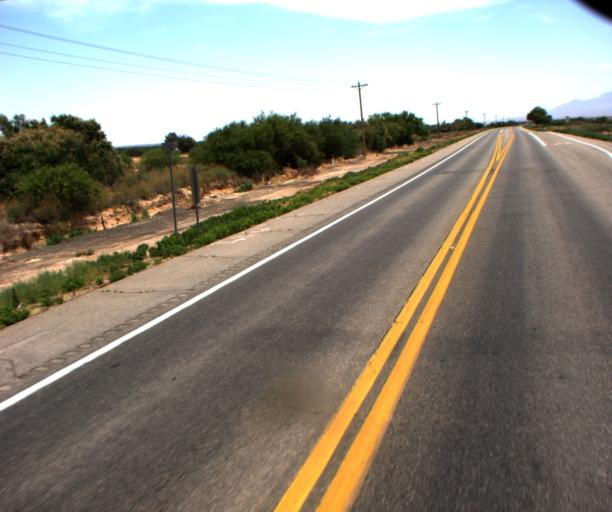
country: US
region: Arizona
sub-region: Graham County
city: Pima
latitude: 32.9922
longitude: -109.9383
